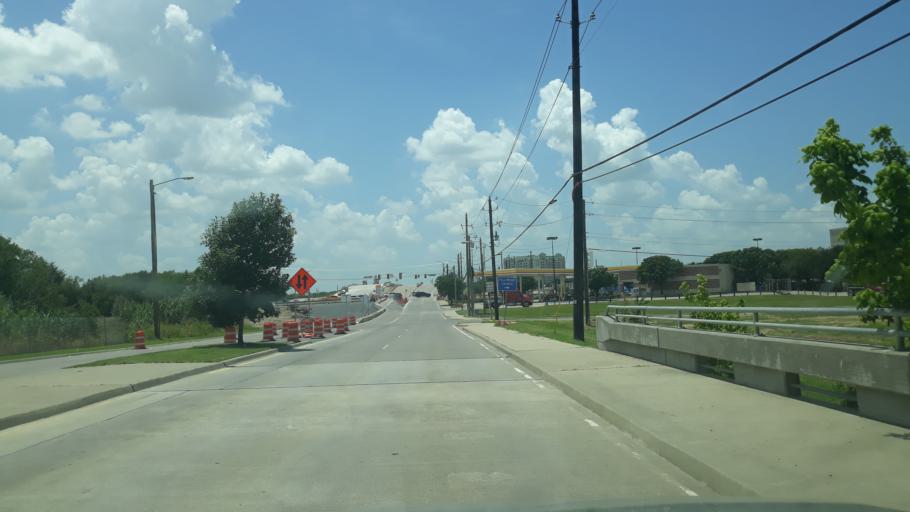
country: US
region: Texas
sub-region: Dallas County
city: Coppell
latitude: 32.9551
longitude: -97.0356
